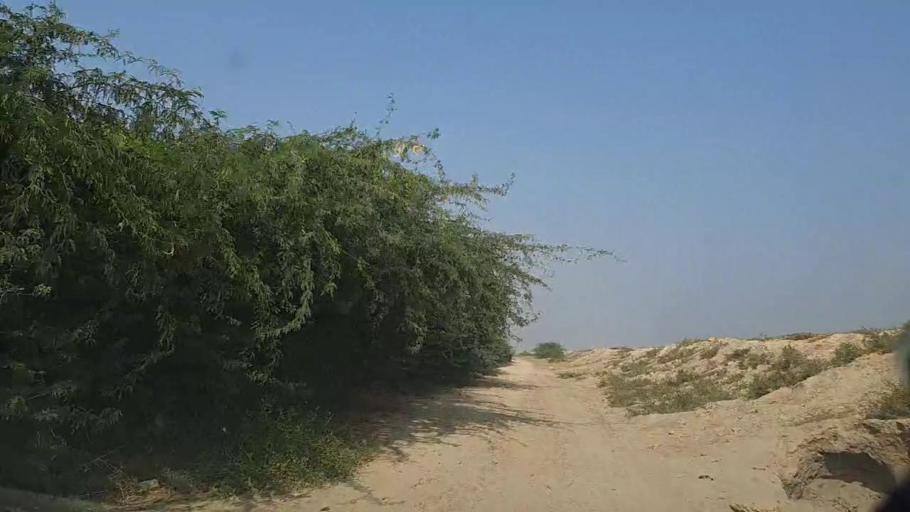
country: PK
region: Sindh
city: Thatta
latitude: 24.6628
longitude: 67.9256
